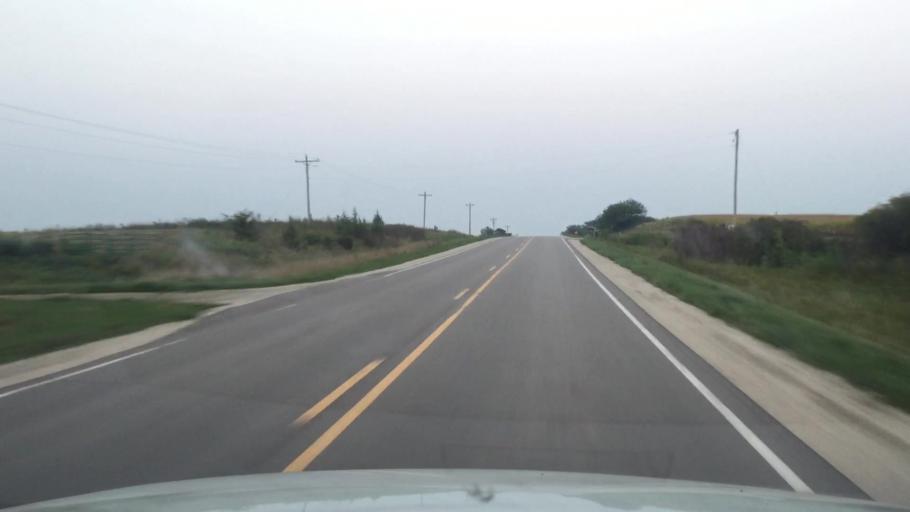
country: US
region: Iowa
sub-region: Warren County
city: Indianola
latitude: 41.1824
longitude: -93.4575
